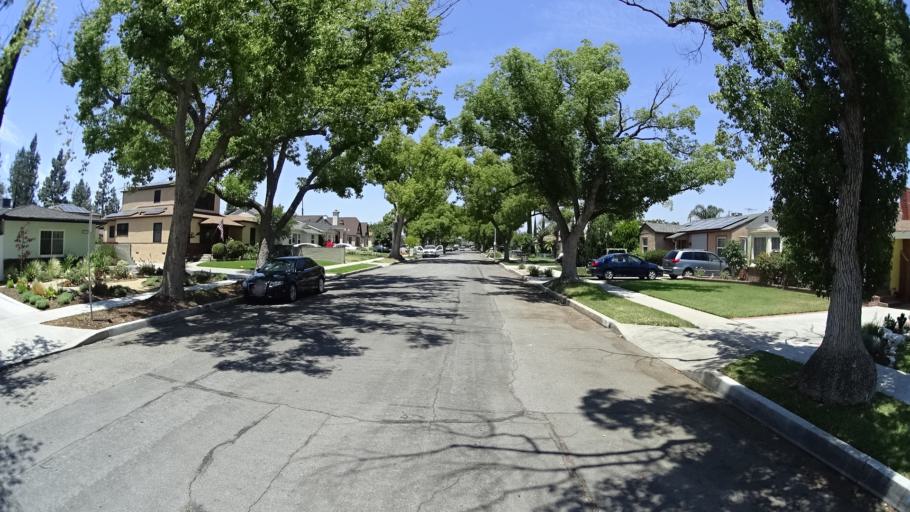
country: US
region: California
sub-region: Los Angeles County
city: Burbank
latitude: 34.1751
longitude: -118.3410
